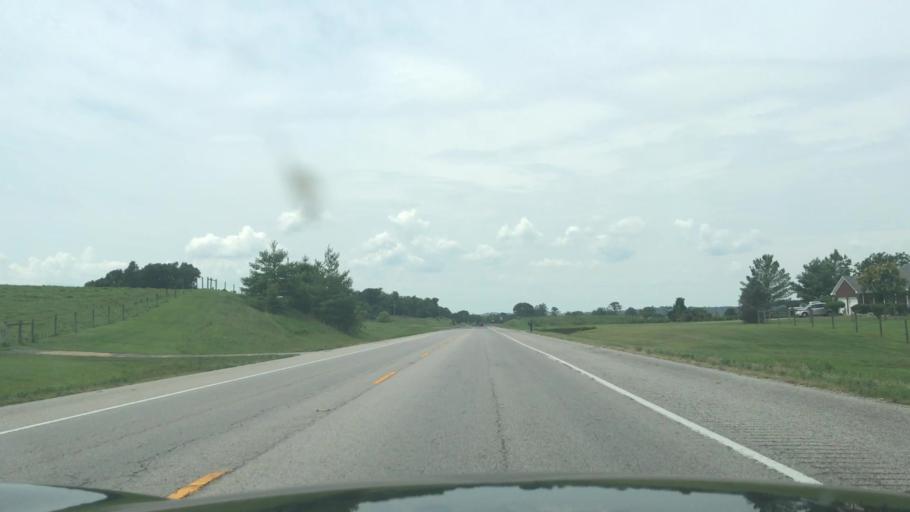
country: US
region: Kentucky
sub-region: Green County
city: Greensburg
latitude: 37.3051
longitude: -85.4394
